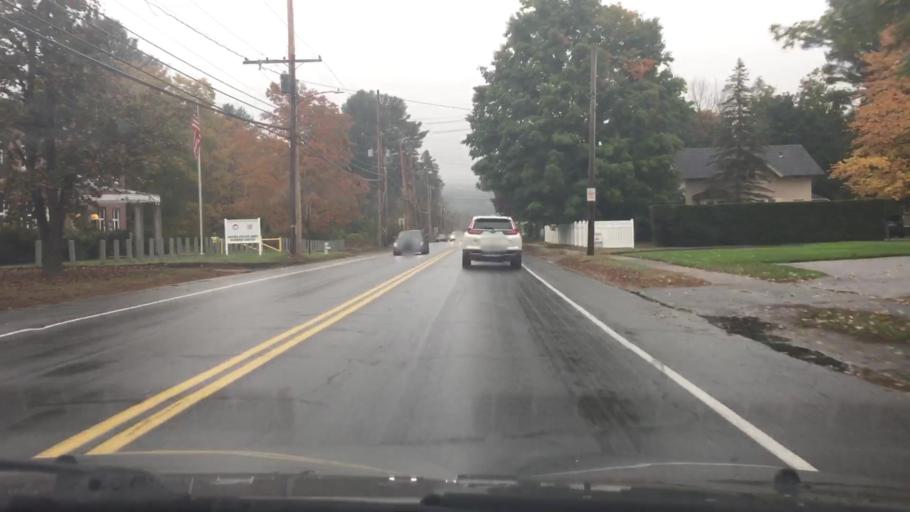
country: US
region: New Hampshire
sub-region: Cheshire County
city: Keene
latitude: 42.9129
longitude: -72.2663
